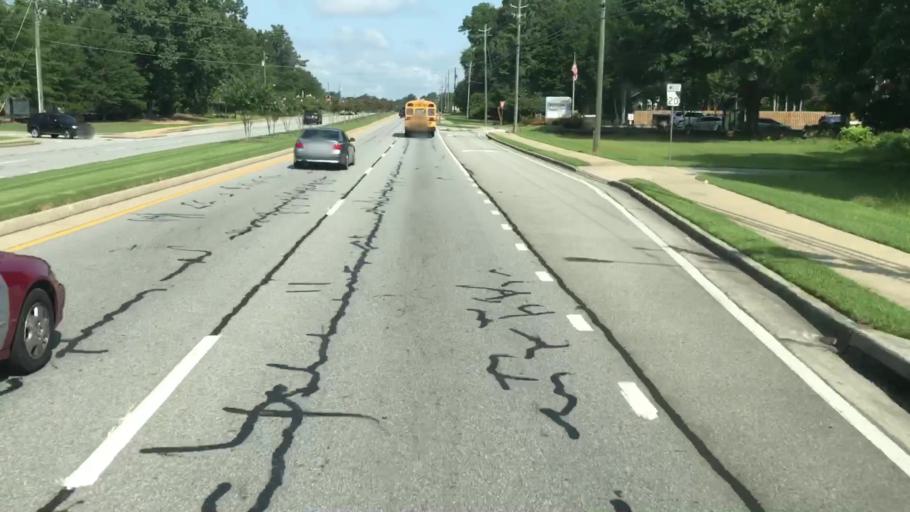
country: US
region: Georgia
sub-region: Gwinnett County
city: Grayson
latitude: 33.8873
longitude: -83.9458
